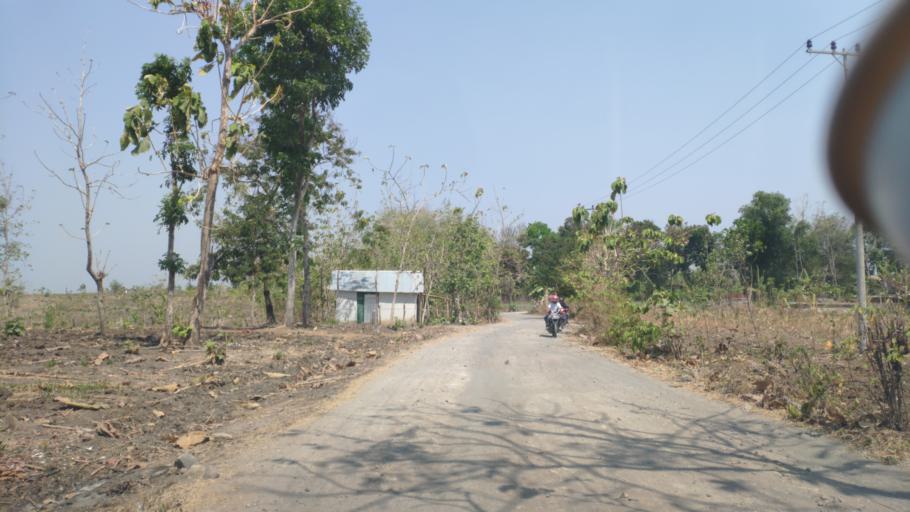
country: ID
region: West Java
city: Ngawi
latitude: -7.3666
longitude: 111.4345
